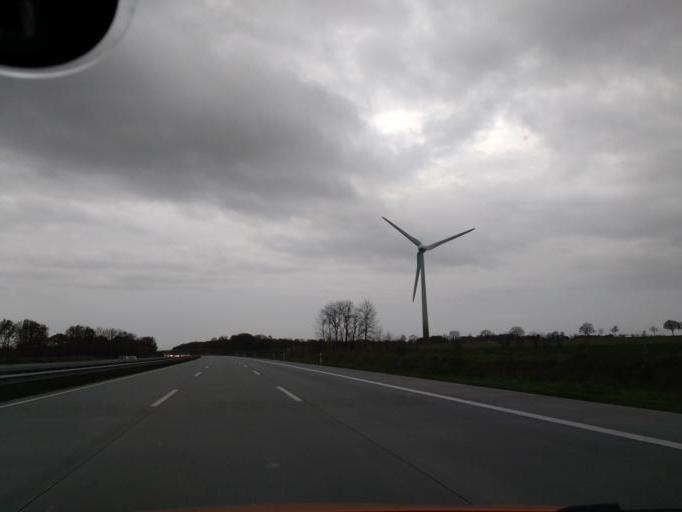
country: DE
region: Lower Saxony
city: Reessum
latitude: 53.1428
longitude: 9.2239
